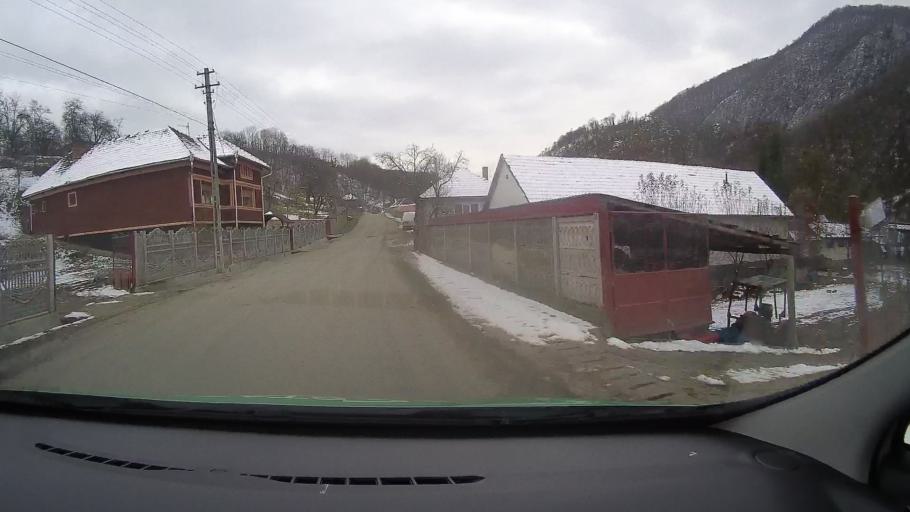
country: RO
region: Hunedoara
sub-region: Comuna Balsa
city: Balsa
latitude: 46.0208
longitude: 23.1448
